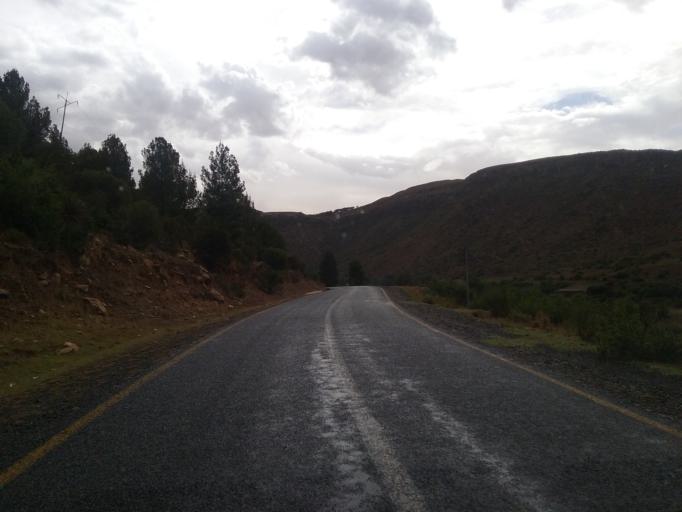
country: LS
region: Quthing
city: Quthing
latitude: -30.3377
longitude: 27.7254
